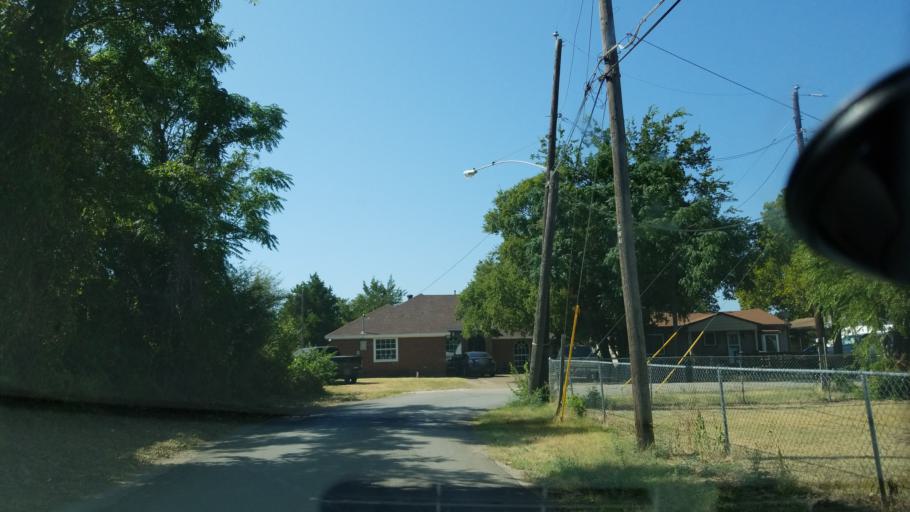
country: US
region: Texas
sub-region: Dallas County
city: Cockrell Hill
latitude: 32.7002
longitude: -96.9195
